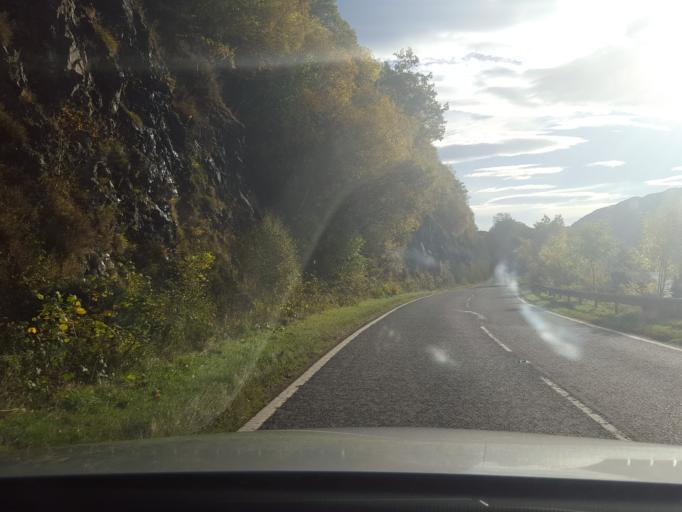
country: GB
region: Scotland
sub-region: Highland
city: Fort William
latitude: 57.2608
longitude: -5.4927
